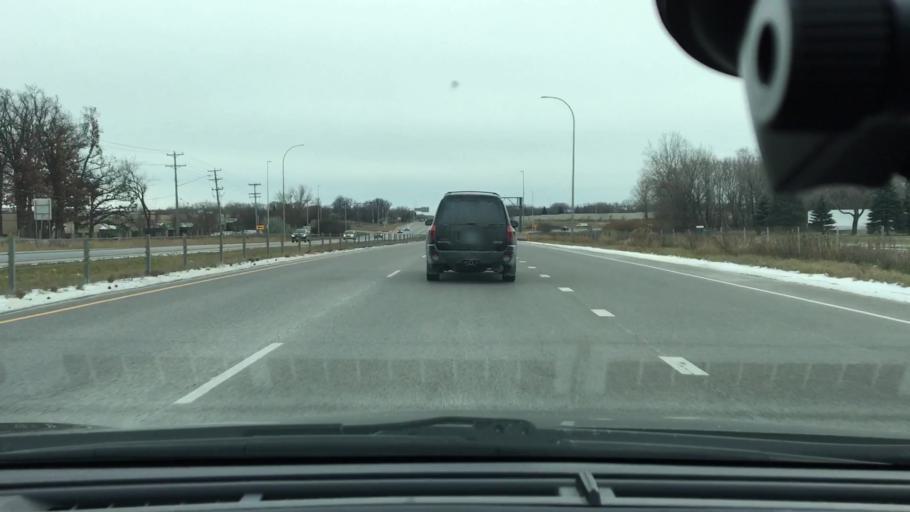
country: US
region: Minnesota
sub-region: Hennepin County
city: Osseo
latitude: 45.0887
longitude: -93.4025
